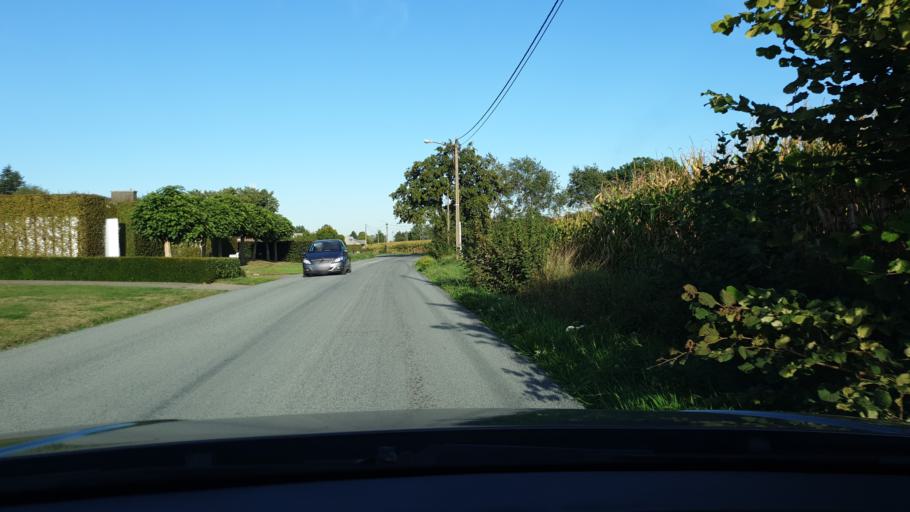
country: BE
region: Flanders
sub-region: Provincie Antwerpen
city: Geel
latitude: 51.1552
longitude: 4.9638
